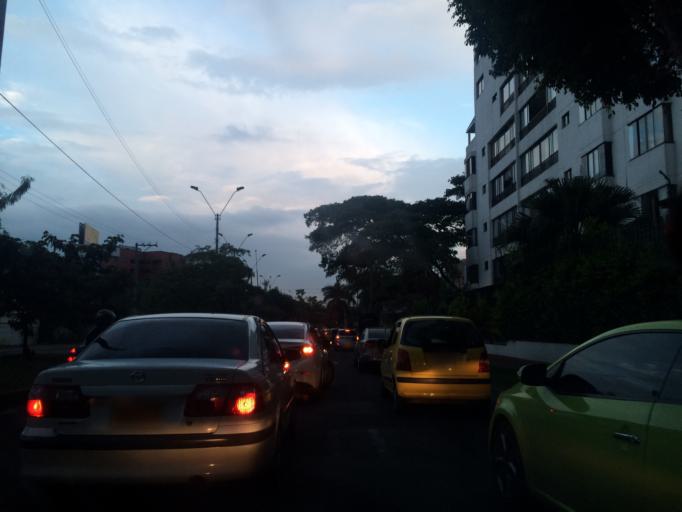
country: CO
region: Valle del Cauca
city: Cali
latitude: 3.3936
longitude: -76.5396
